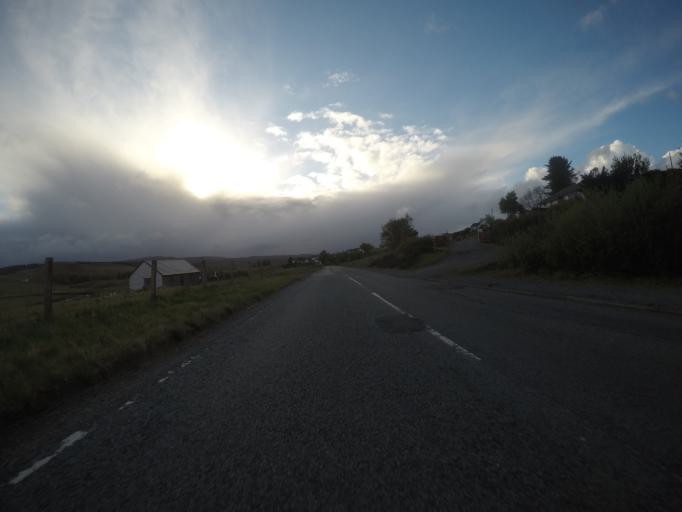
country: GB
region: Scotland
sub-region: Highland
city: Isle of Skye
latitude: 57.4525
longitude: -6.2924
